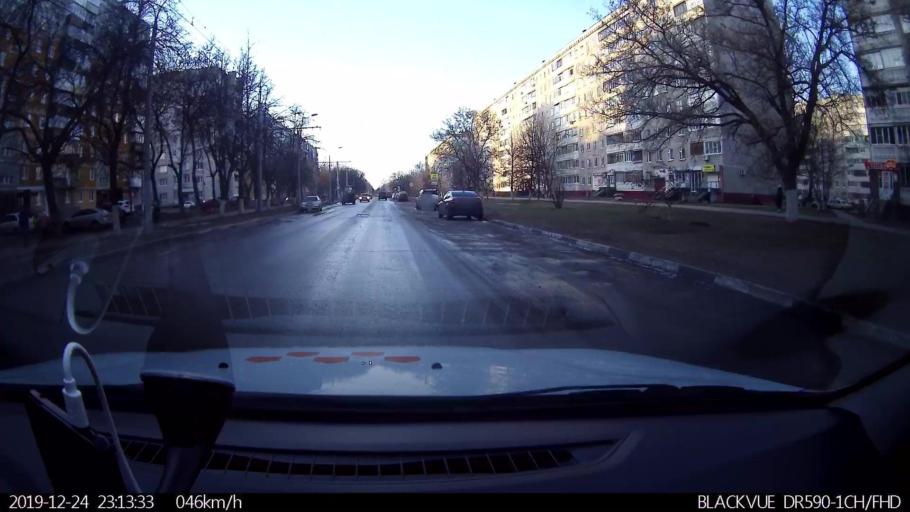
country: RU
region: Nizjnij Novgorod
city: Gorbatovka
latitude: 56.2524
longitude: 43.8611
